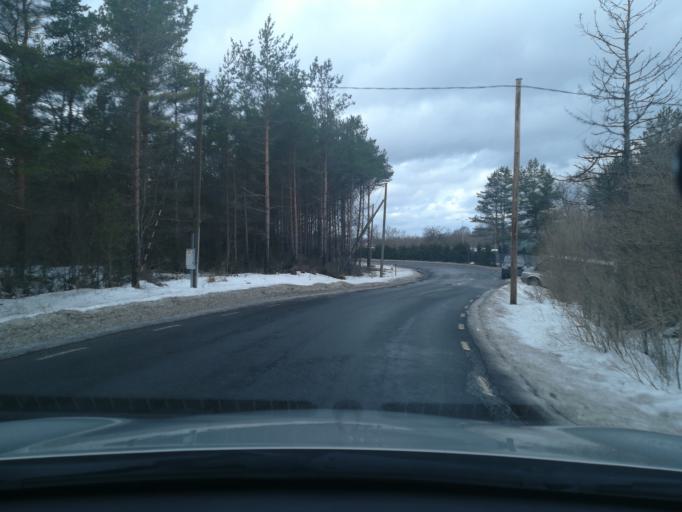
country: EE
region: Harju
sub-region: Saue linn
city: Saue
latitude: 59.3627
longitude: 24.5182
